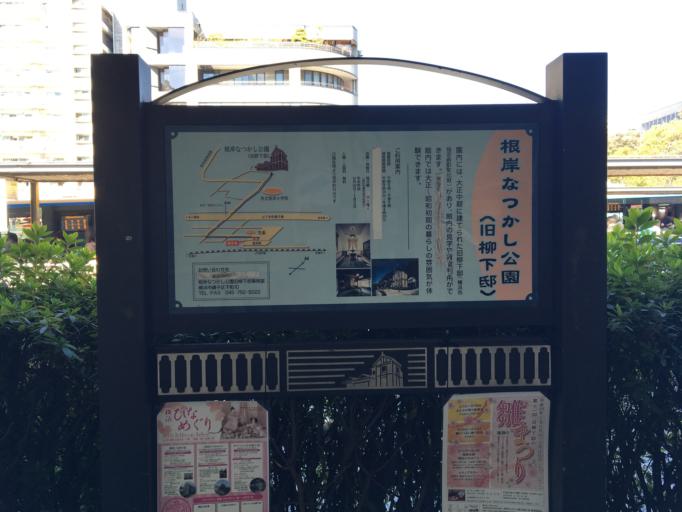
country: JP
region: Kanagawa
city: Yokohama
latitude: 35.4159
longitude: 139.6349
